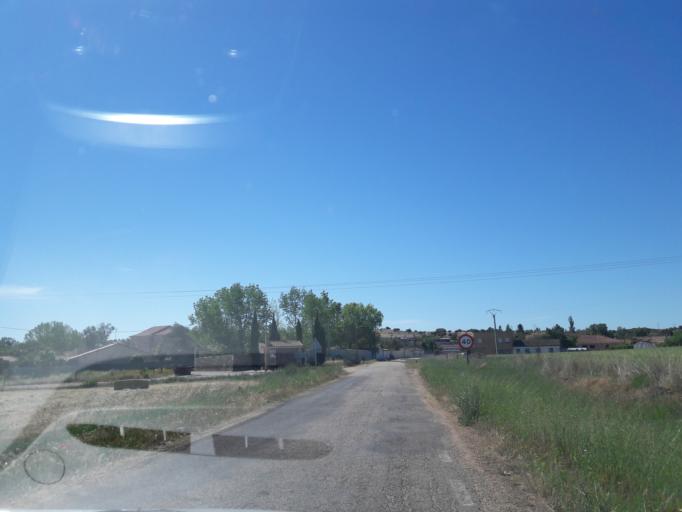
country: ES
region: Castille and Leon
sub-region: Provincia de Salamanca
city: Zarapicos
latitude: 41.0397
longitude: -5.8462
